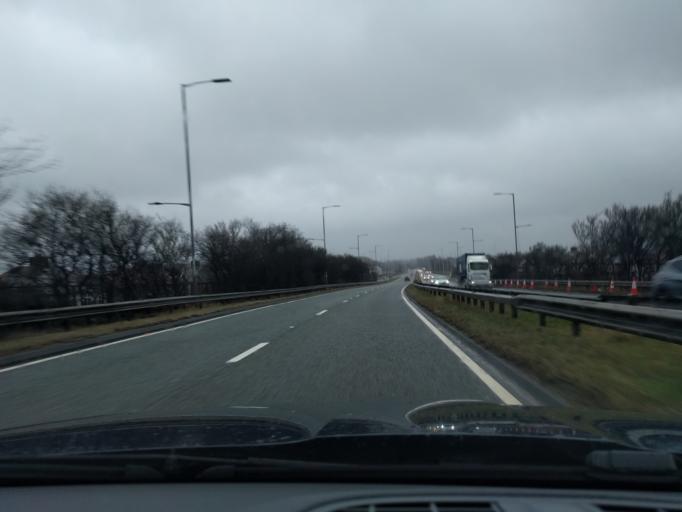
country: GB
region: England
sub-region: South Tyneside
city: Jarrow
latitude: 54.9663
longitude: -1.4742
